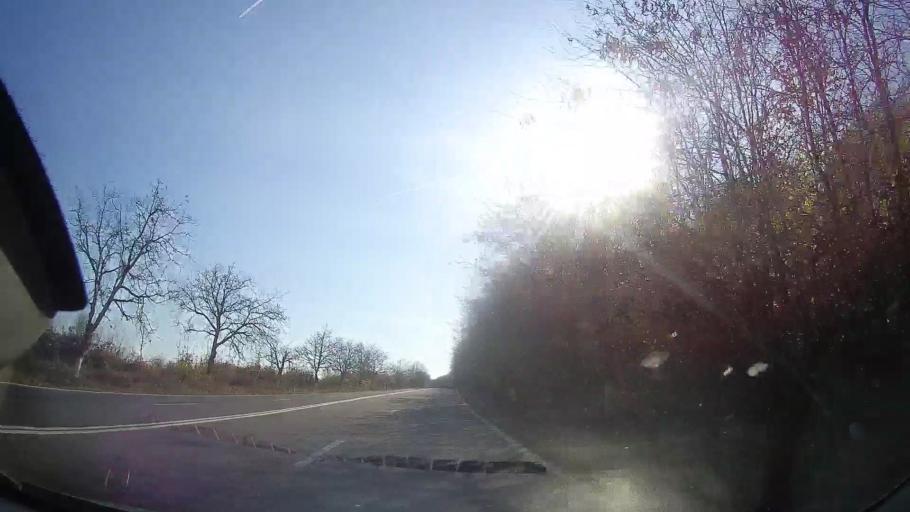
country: RO
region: Constanta
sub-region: Comuna Douazeci si Trei August
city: Dulcesti
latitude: 43.8866
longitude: 28.5732
